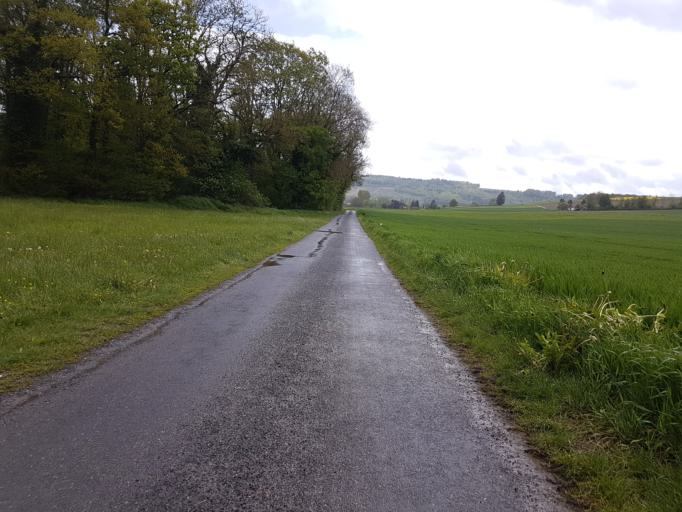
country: CH
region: Vaud
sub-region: Morges District
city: La Sarraz
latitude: 46.6494
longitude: 6.5184
